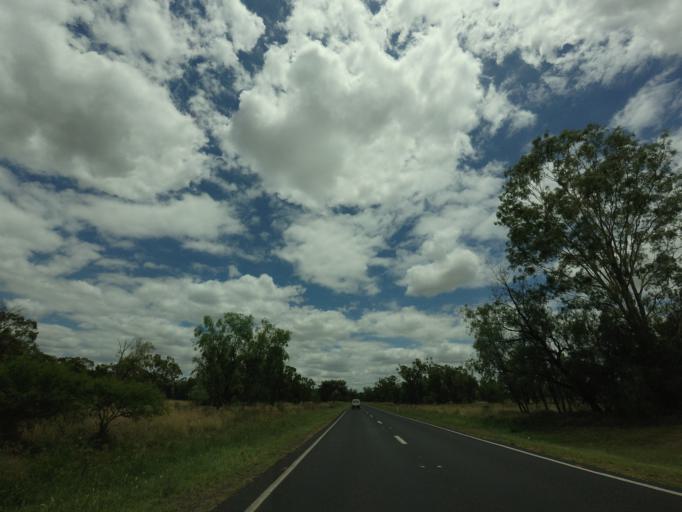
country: AU
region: New South Wales
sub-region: Moree Plains
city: Boggabilla
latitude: -28.5874
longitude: 150.3494
